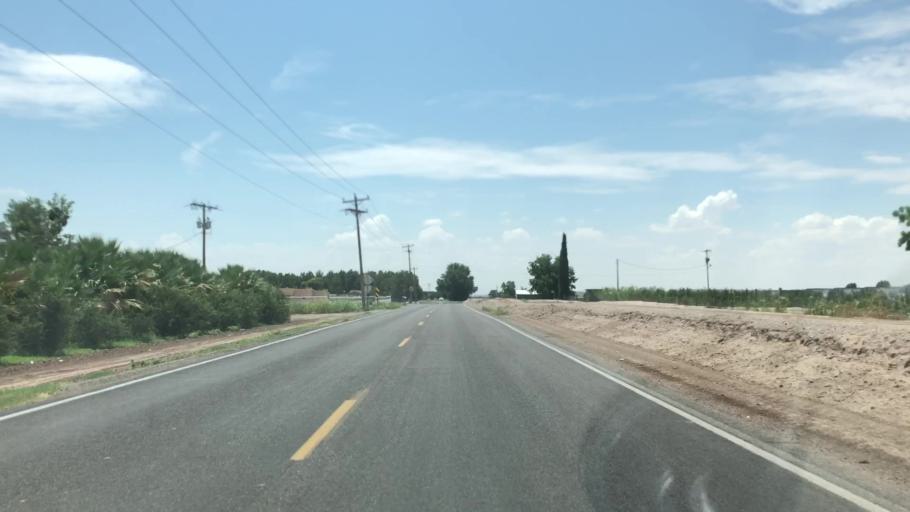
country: US
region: New Mexico
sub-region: Dona Ana County
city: Vado
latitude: 32.0877
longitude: -106.6835
